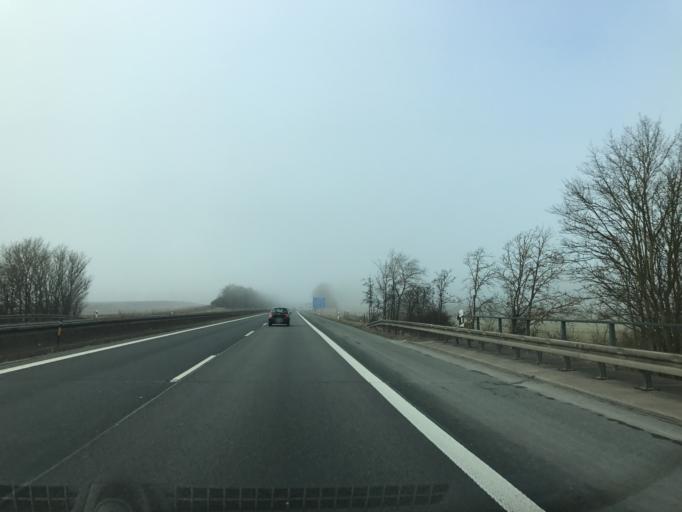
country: DE
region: Bavaria
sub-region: Regierungsbezirk Mittelfranken
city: Herrieden
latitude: 49.2569
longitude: 10.4940
